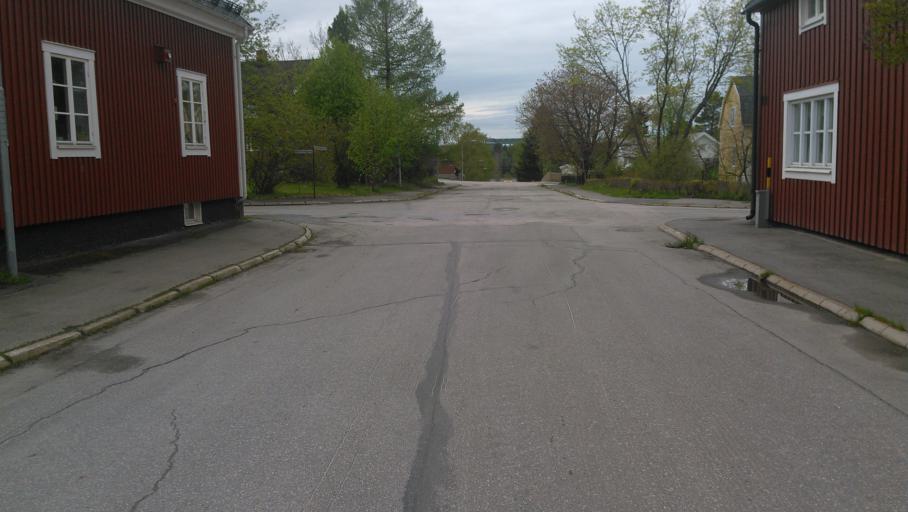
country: SE
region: Vaesterbotten
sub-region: Umea Kommun
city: Umea
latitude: 63.8048
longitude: 20.3054
